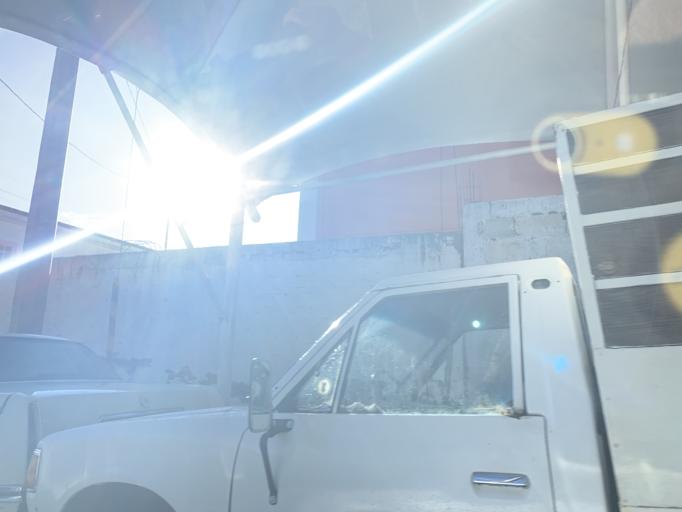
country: MX
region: Puebla
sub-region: Cuautlancingo
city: Sanctorum
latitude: 19.0807
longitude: -98.2441
